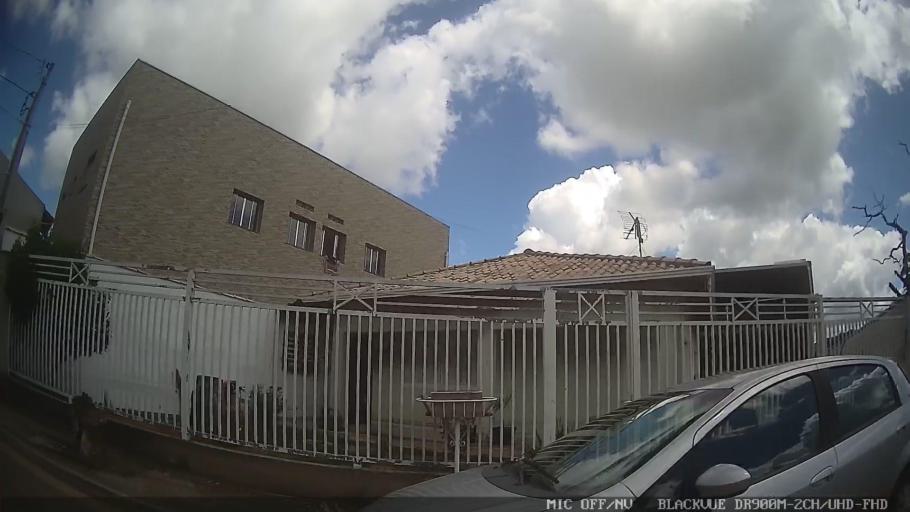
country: BR
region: Minas Gerais
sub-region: Extrema
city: Extrema
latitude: -22.8667
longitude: -46.3401
